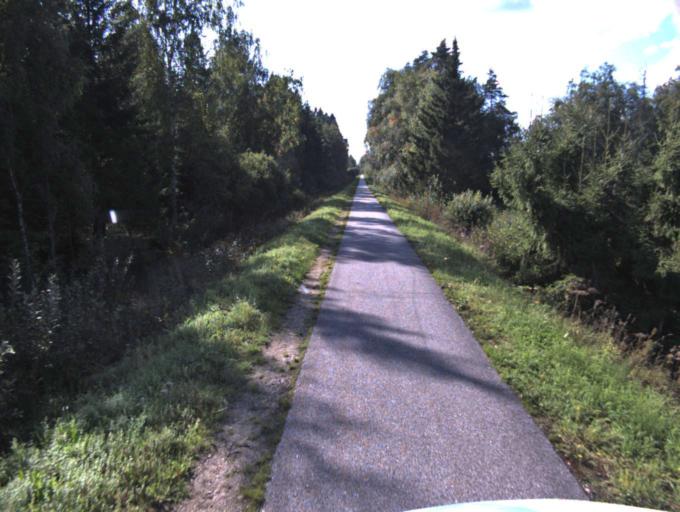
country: SE
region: Vaestra Goetaland
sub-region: Ulricehamns Kommun
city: Ulricehamn
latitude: 57.8355
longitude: 13.2349
